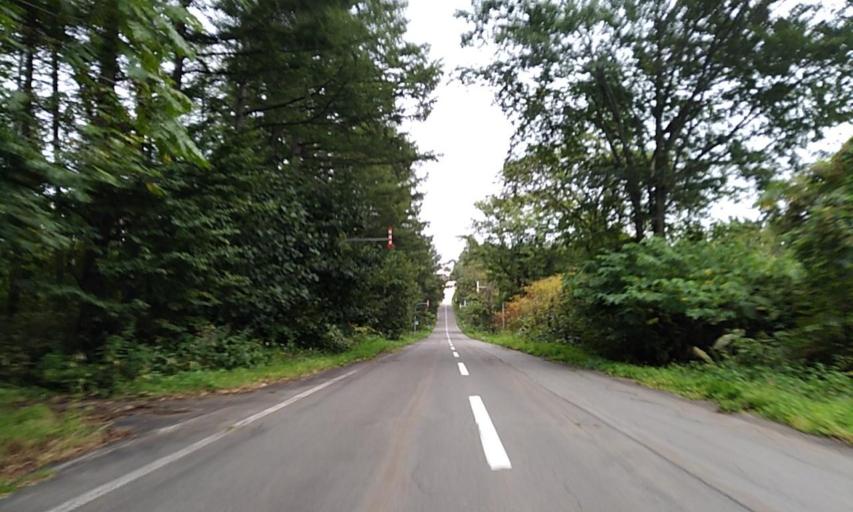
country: JP
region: Hokkaido
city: Obihiro
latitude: 42.6690
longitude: 143.0585
